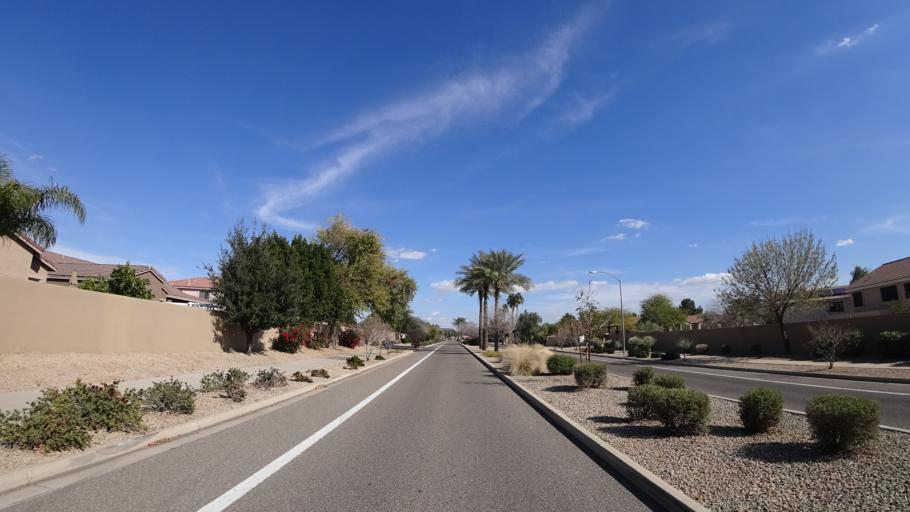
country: US
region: Arizona
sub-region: Maricopa County
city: Peoria
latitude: 33.6719
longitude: -112.2061
